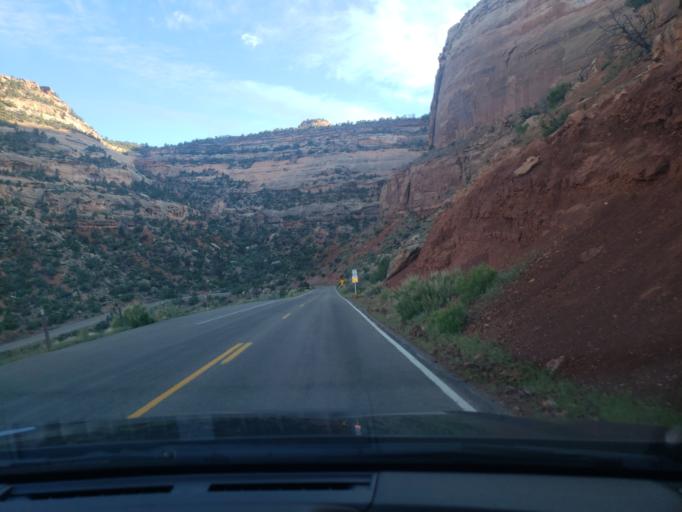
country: US
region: Colorado
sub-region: Mesa County
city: Fruita
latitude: 39.1105
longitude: -108.7353
